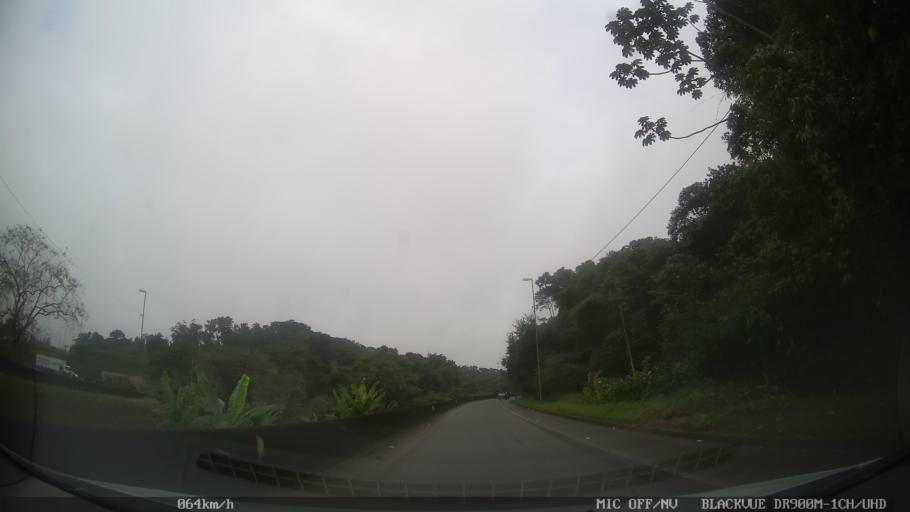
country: BR
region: Santa Catarina
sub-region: Joinville
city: Joinville
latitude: -26.3842
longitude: -48.8462
